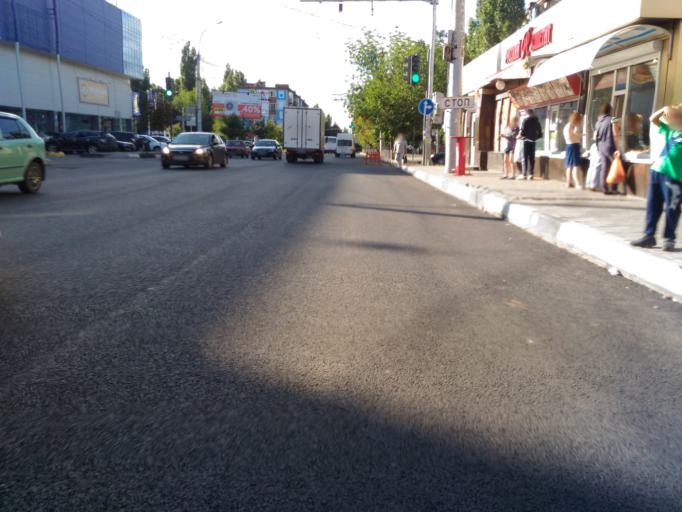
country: RU
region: Voronezj
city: Voronezh
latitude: 51.6528
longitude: 39.1499
